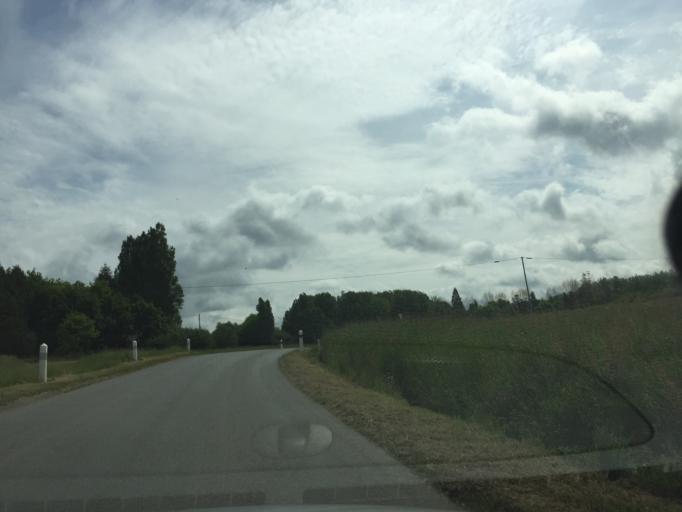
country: FR
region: Brittany
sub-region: Departement des Cotes-d'Armor
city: Corseul
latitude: 48.5262
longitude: -2.1601
